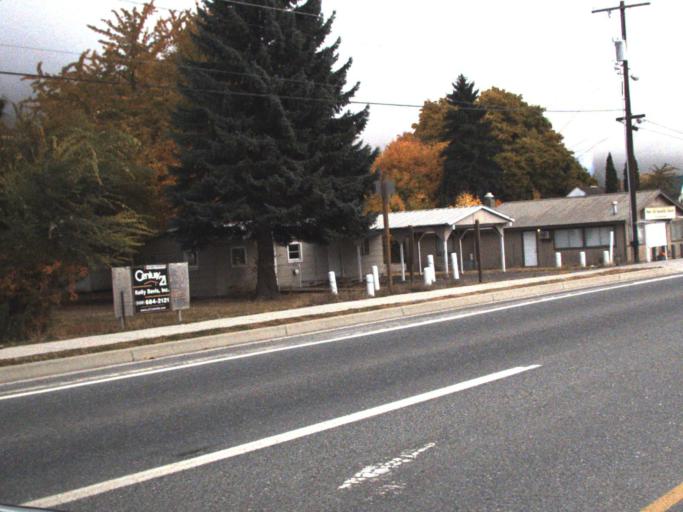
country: US
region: Washington
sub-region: Stevens County
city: Kettle Falls
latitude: 48.6107
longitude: -118.0607
